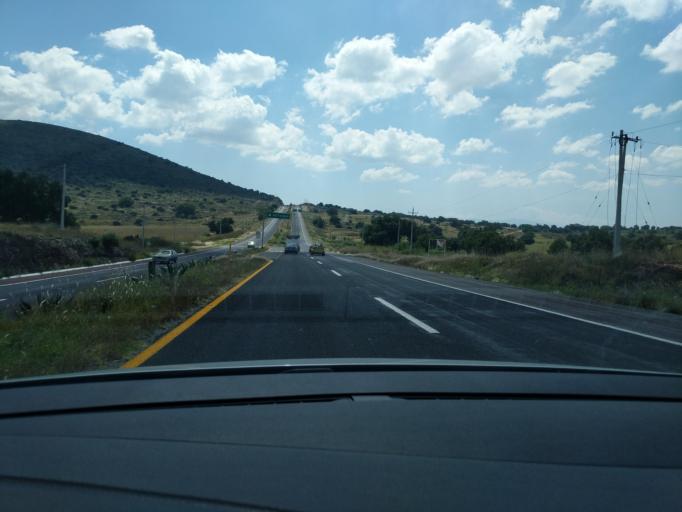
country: MX
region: Hidalgo
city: Zempoala
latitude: 19.8994
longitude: -98.6720
